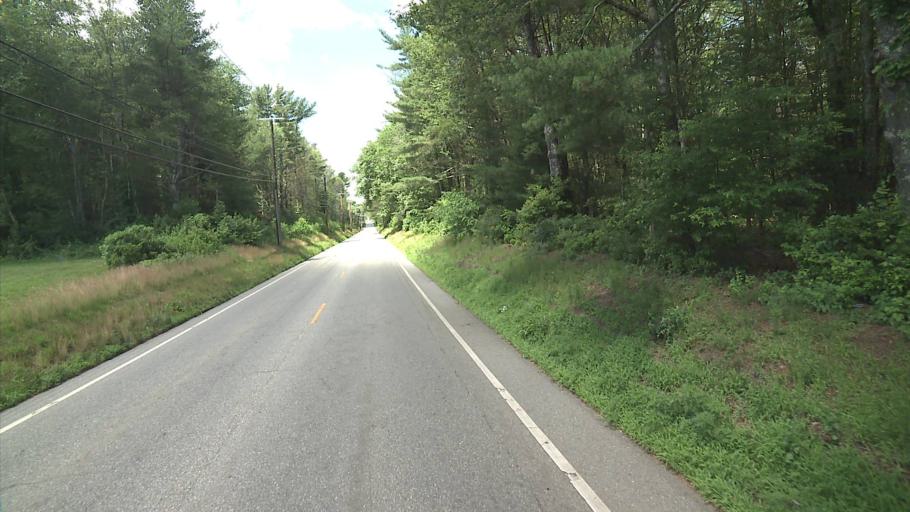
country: US
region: Rhode Island
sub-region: Washington County
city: Ashaway
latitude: 41.4358
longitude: -71.8211
